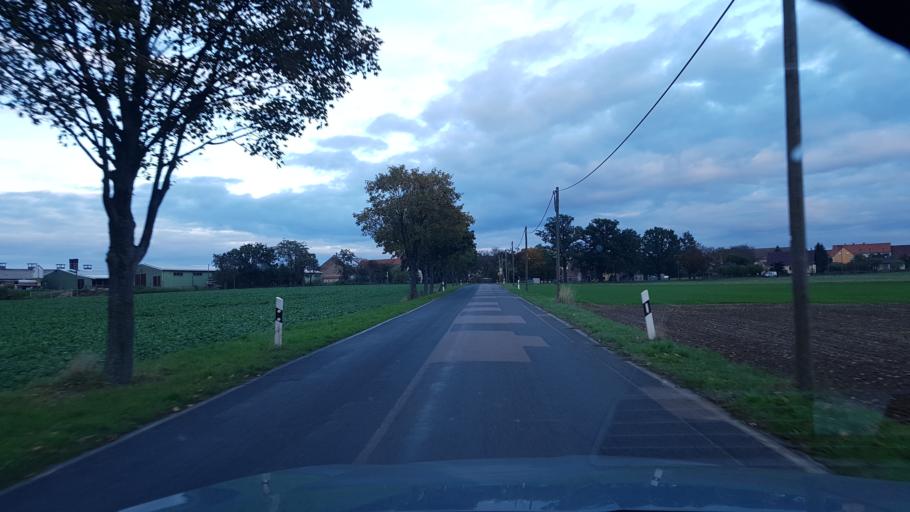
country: DE
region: Saxony
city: Grossenhain
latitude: 51.2480
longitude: 13.5765
